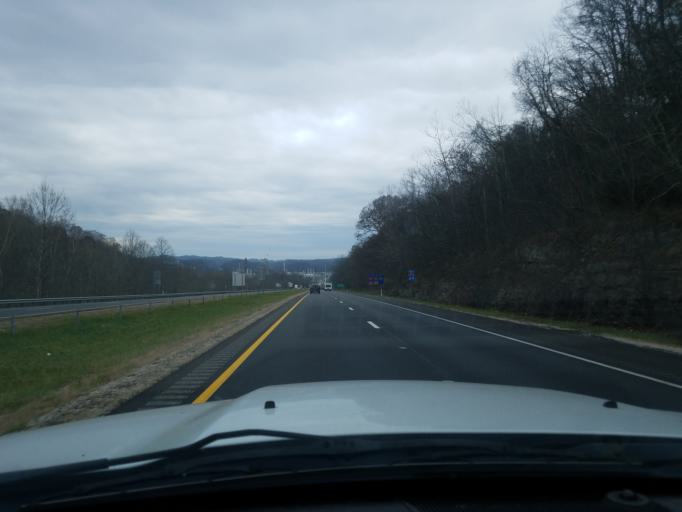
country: US
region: West Virginia
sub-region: Wayne County
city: Kenova
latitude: 38.3856
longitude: -82.5846
